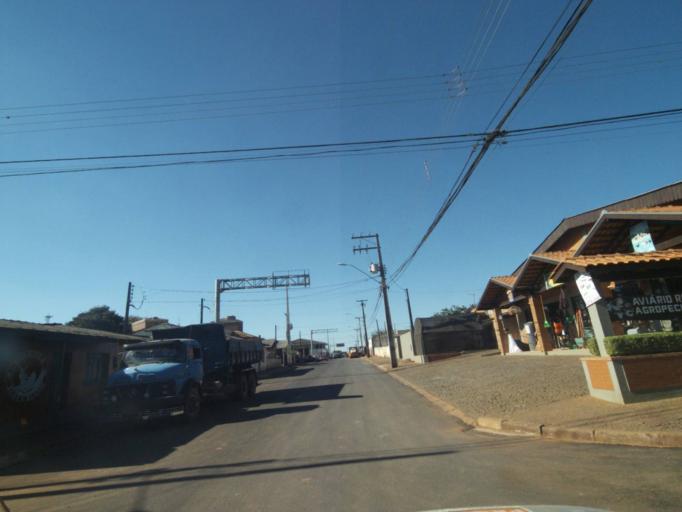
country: BR
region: Parana
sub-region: Tibagi
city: Tibagi
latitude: -24.5198
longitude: -50.4133
